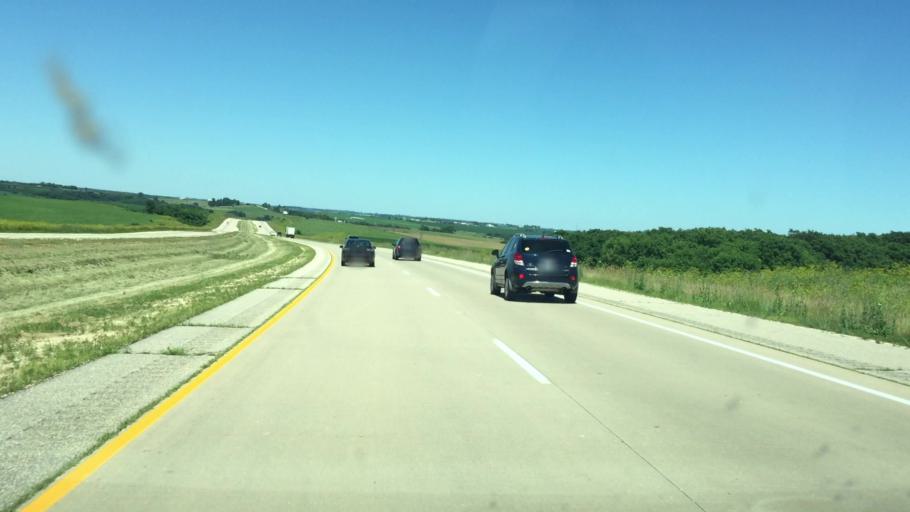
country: US
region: Wisconsin
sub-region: Iowa County
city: Mineral Point
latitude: 42.7974
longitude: -90.2797
